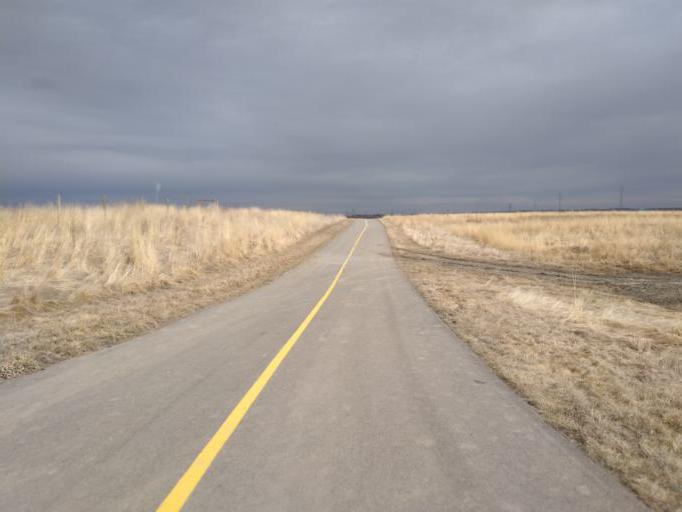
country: CA
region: Alberta
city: Airdrie
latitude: 51.1796
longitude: -114.0370
